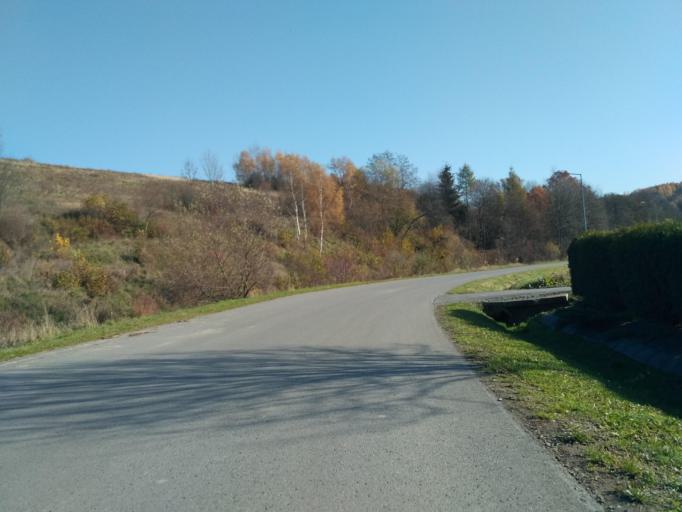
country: PL
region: Subcarpathian Voivodeship
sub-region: Powiat brzozowski
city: Nozdrzec
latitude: 49.7939
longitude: 22.1822
